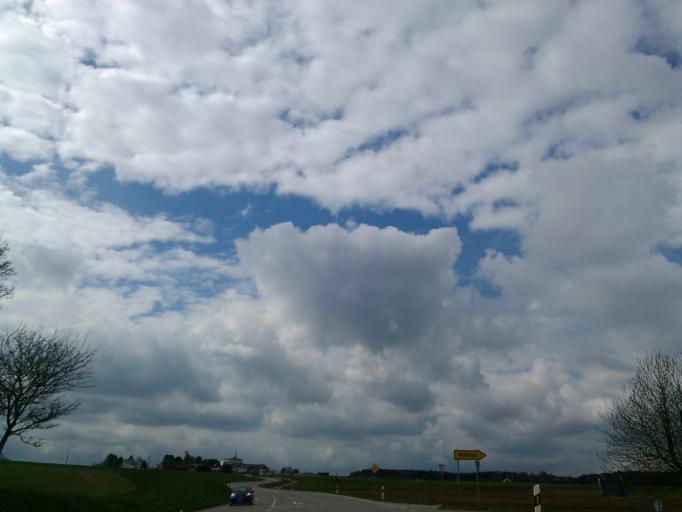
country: DE
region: Baden-Wuerttemberg
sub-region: Tuebingen Region
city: Bernstadt
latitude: 48.4638
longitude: 10.0362
